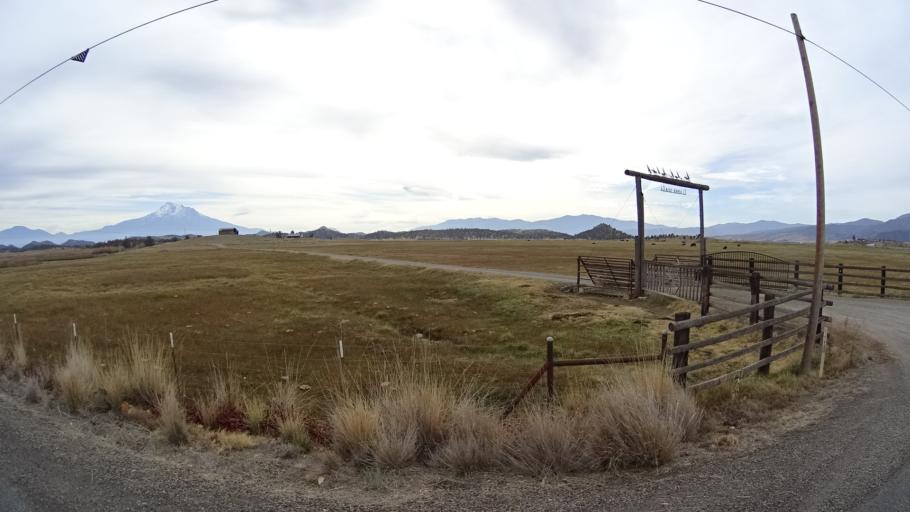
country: US
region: California
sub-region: Siskiyou County
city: Montague
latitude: 41.6478
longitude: -122.5018
